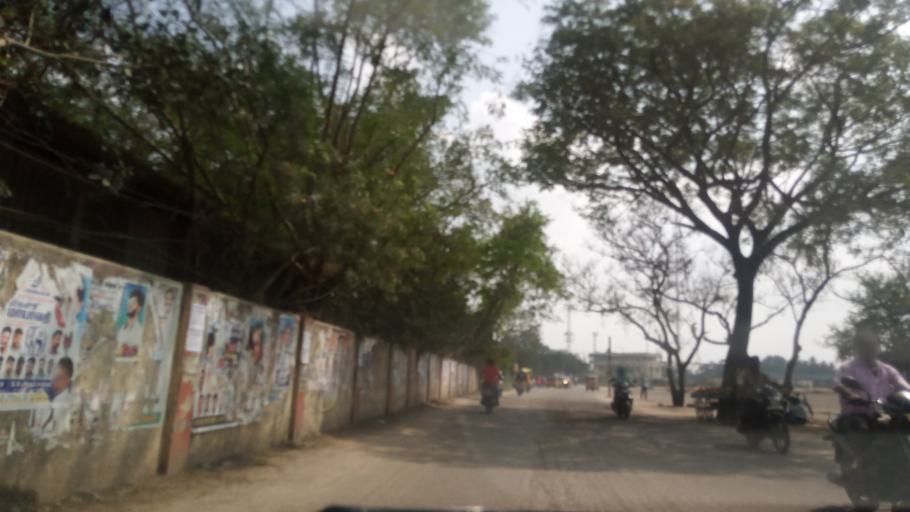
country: IN
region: Tamil Nadu
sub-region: Vellore
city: Arakkonam
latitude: 13.0831
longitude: 79.6644
